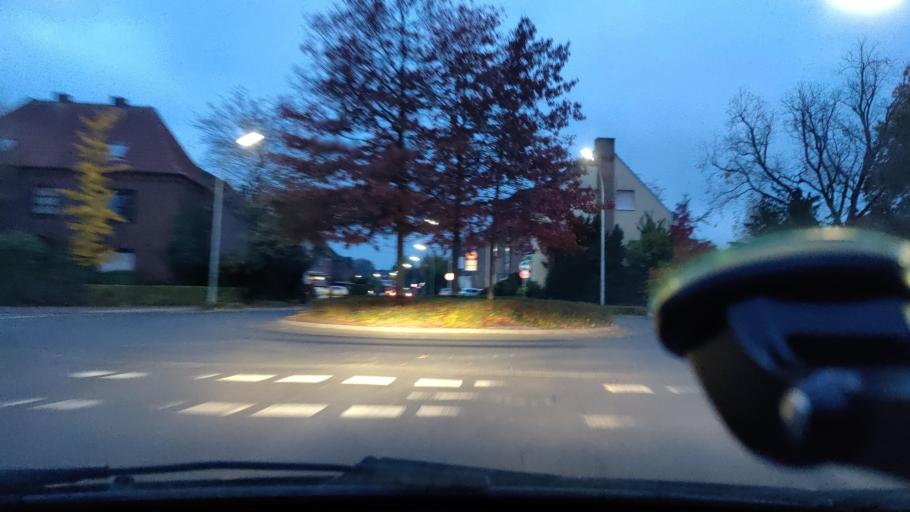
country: DE
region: North Rhine-Westphalia
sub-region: Regierungsbezirk Dusseldorf
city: Xanten
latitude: 51.6558
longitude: 6.4569
